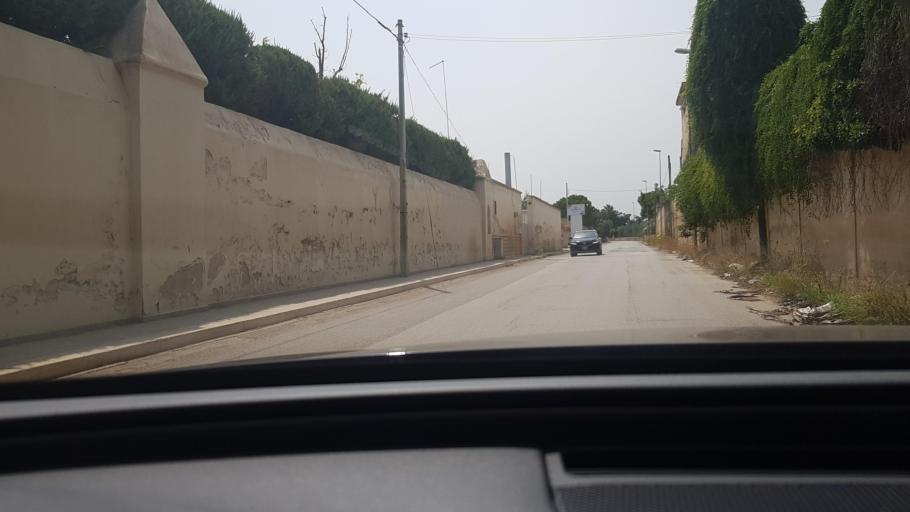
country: IT
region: Apulia
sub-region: Provincia di Barletta - Andria - Trani
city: Andria
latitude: 41.2316
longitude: 16.2684
